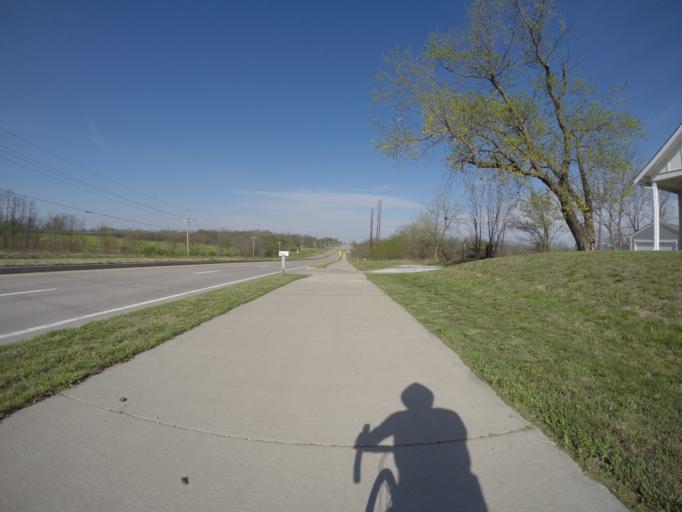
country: US
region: Missouri
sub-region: Cass County
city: Raymore
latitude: 38.8550
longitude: -94.4520
